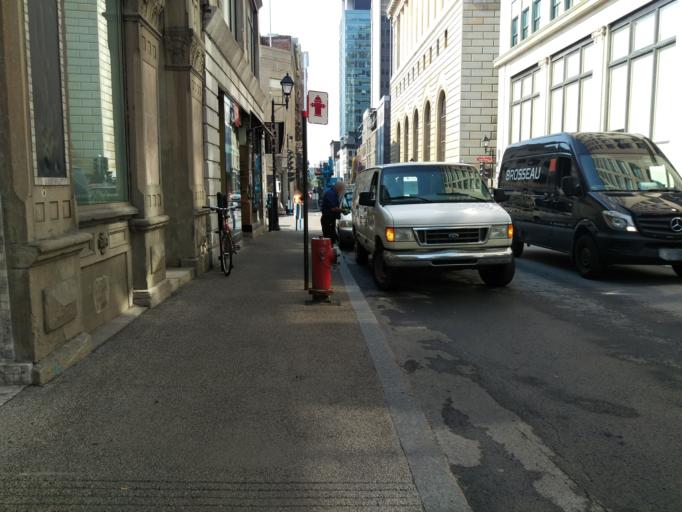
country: CA
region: Quebec
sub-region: Montreal
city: Montreal
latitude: 45.5027
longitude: -73.5585
